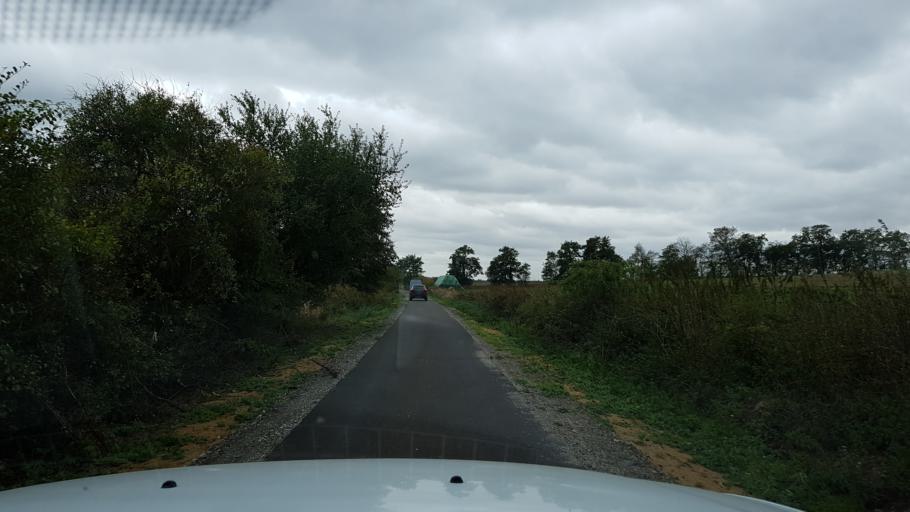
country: PL
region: West Pomeranian Voivodeship
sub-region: Powiat gryfinski
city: Cedynia
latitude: 52.8588
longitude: 14.2837
